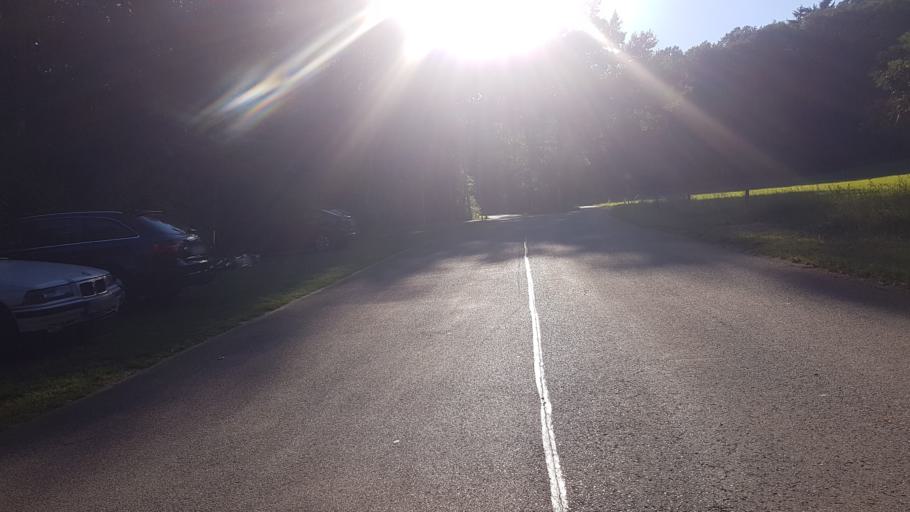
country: DE
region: Bavaria
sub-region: Regierungsbezirk Mittelfranken
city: Absberg
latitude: 49.1402
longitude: 10.8918
